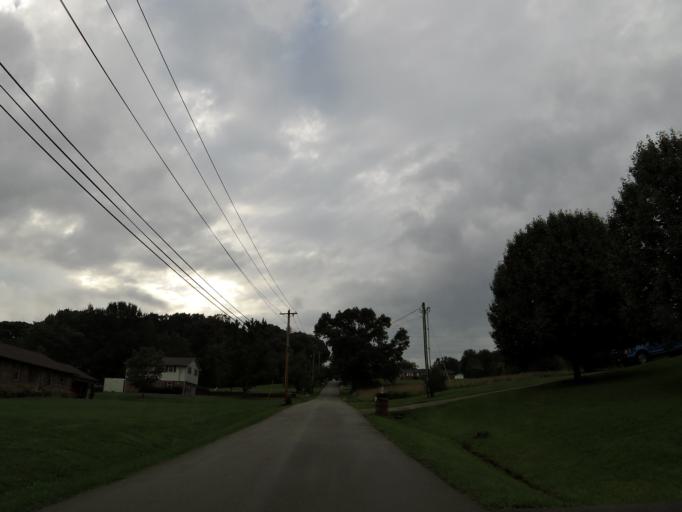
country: US
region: Tennessee
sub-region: Blount County
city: Eagleton Village
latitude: 35.7930
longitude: -83.9144
